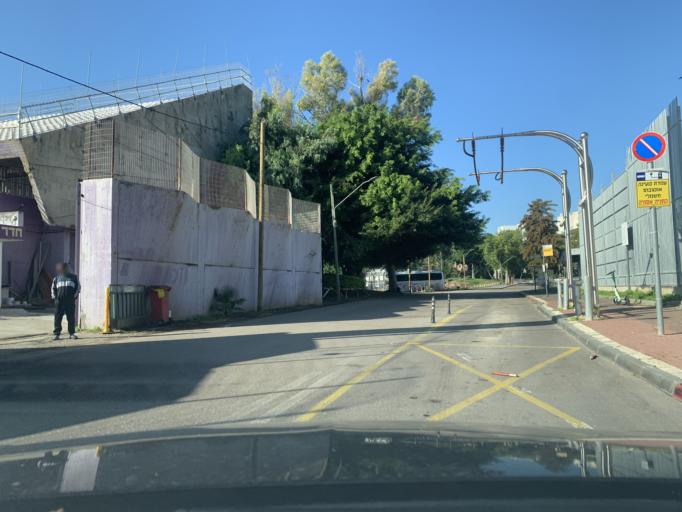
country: IL
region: Tel Aviv
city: Azor
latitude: 32.0460
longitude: 34.8152
